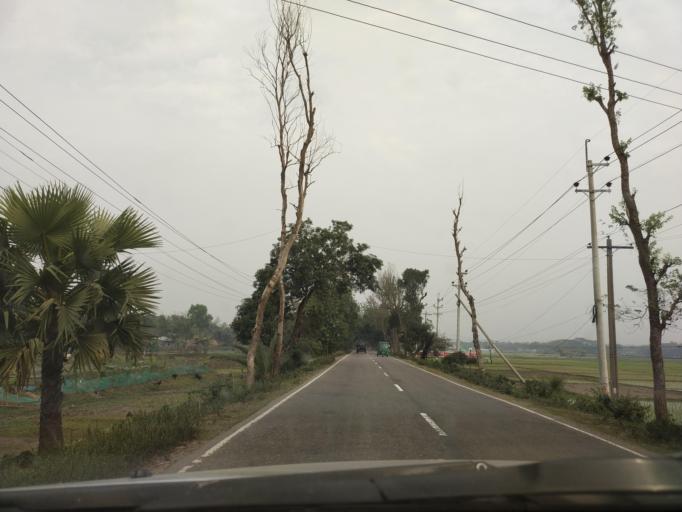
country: BD
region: Dhaka
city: Narsingdi
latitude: 24.0013
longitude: 90.7377
